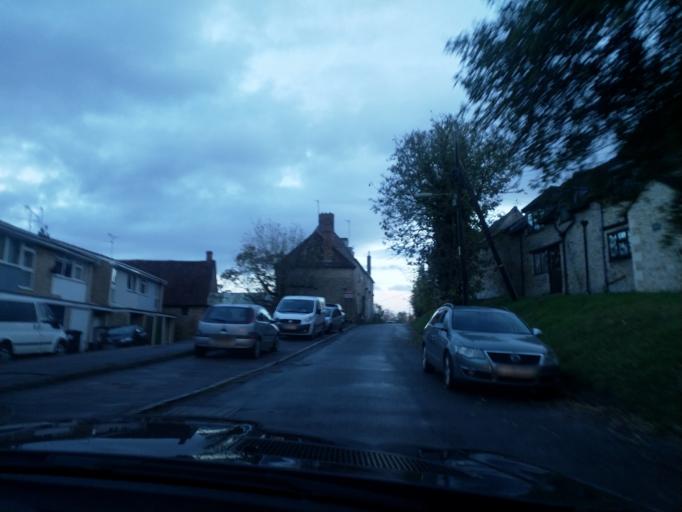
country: GB
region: England
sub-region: Oxfordshire
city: Wheatley
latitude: 51.7463
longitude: -1.1343
